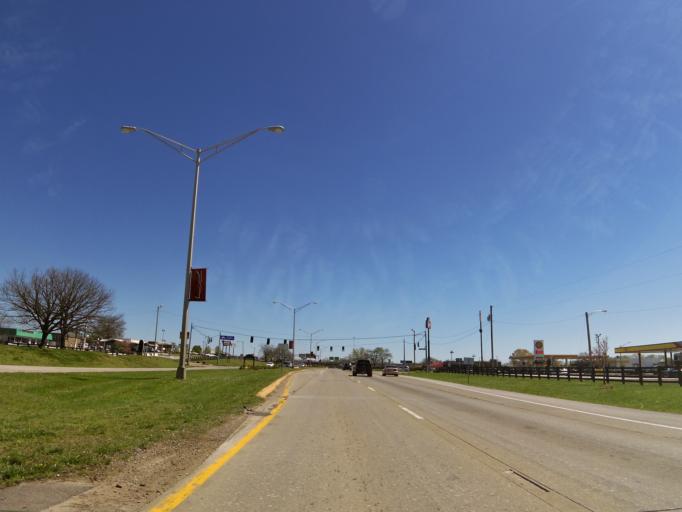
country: US
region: Kentucky
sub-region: Warren County
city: Bowling Green
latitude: 37.0084
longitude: -86.3757
